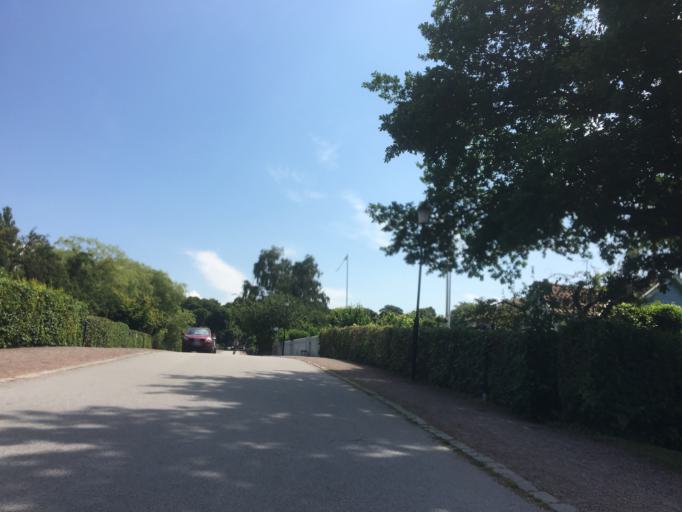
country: SE
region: Skane
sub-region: Landskrona
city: Landskrona
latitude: 55.8747
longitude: 12.8269
